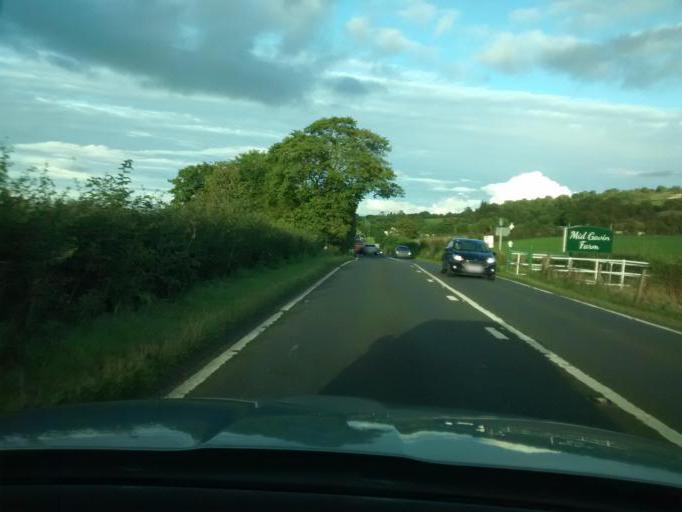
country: GB
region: Scotland
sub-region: Renfrewshire
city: Howwood
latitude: 55.8040
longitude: -4.5808
